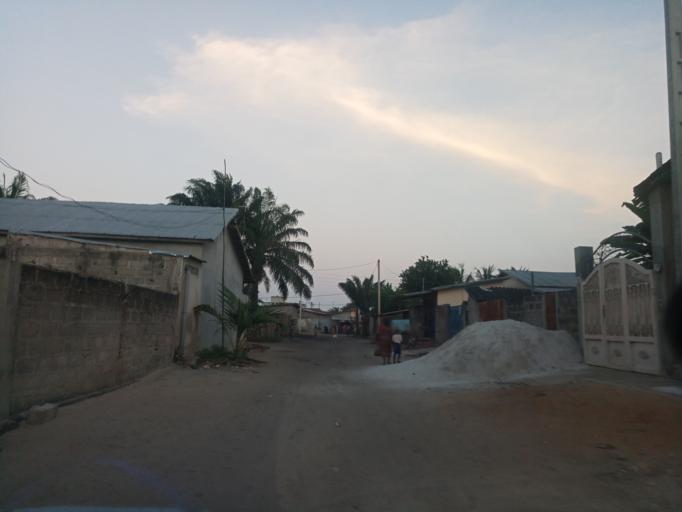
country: BJ
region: Atlantique
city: Hevie
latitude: 6.3927
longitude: 2.2898
